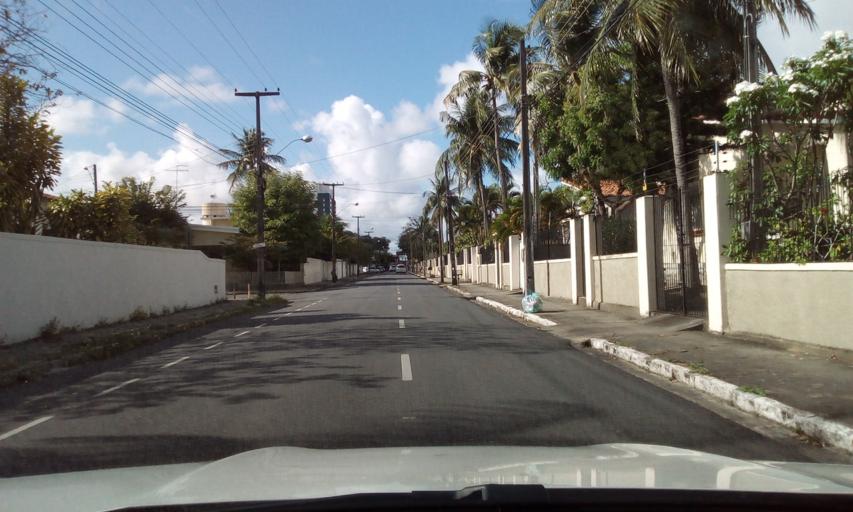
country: BR
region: Paraiba
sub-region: Joao Pessoa
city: Joao Pessoa
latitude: -7.1172
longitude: -34.8495
